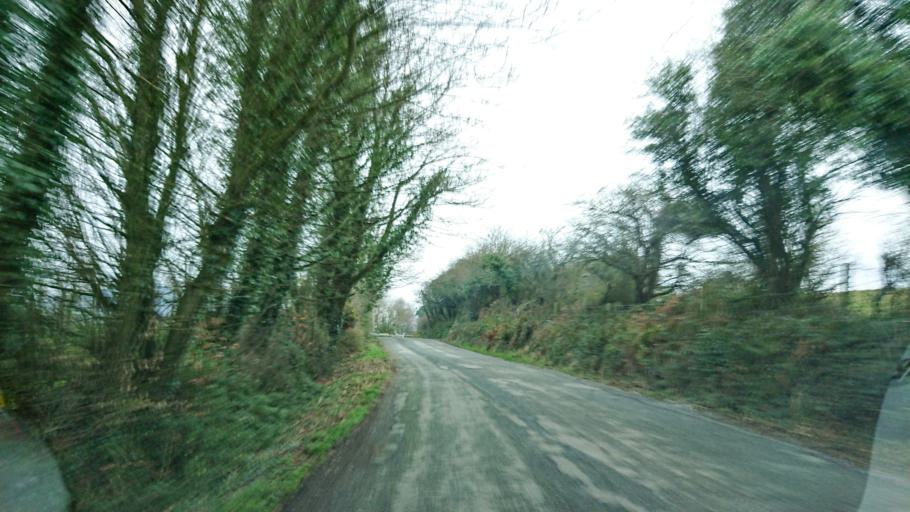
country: IE
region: Munster
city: Carrick-on-Suir
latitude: 52.2760
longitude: -7.4162
